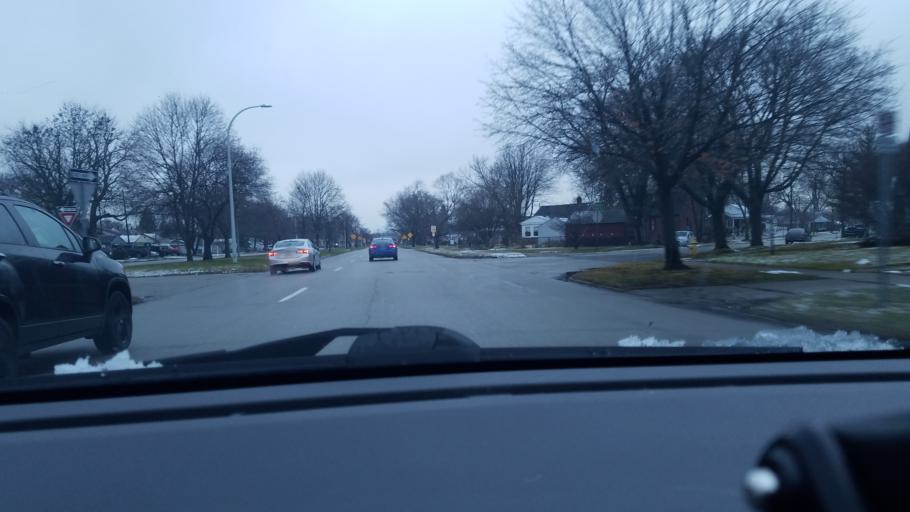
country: US
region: Michigan
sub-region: Wayne County
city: Dearborn Heights
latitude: 42.2964
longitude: -83.2587
